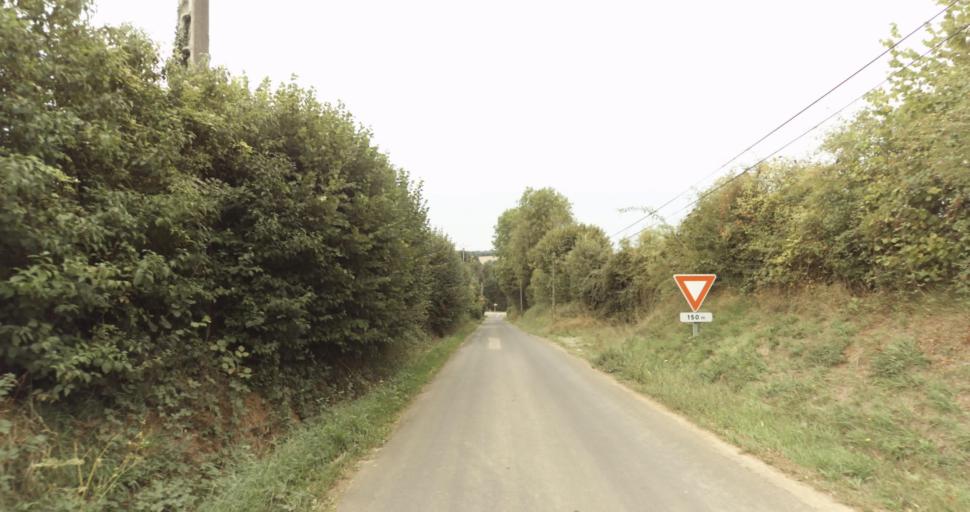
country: FR
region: Lower Normandy
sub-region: Departement de l'Orne
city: Gace
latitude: 48.7617
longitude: 0.3405
